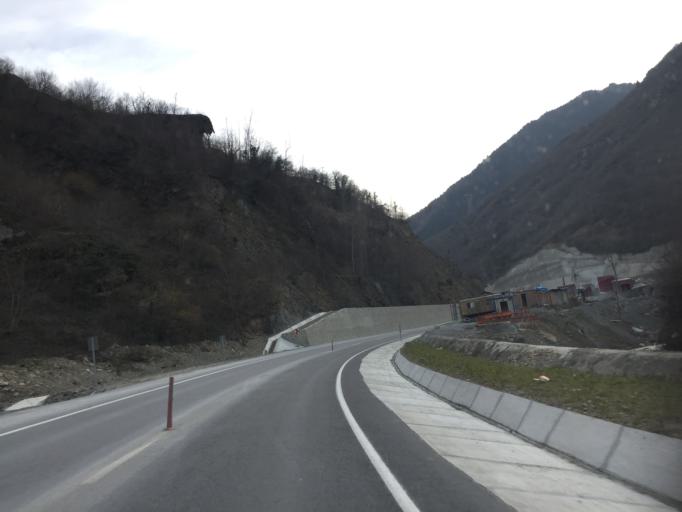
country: TR
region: Trabzon
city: Macka
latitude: 40.7679
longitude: 39.5656
